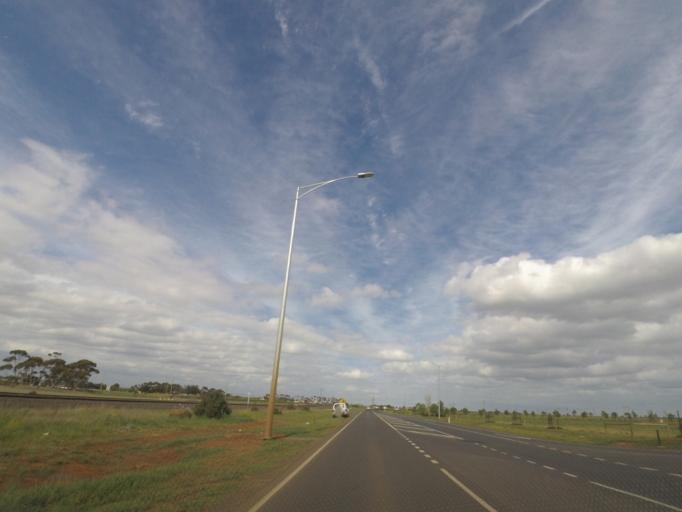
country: AU
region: Victoria
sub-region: Melton
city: Rockbank
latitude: -37.7505
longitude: 144.6990
